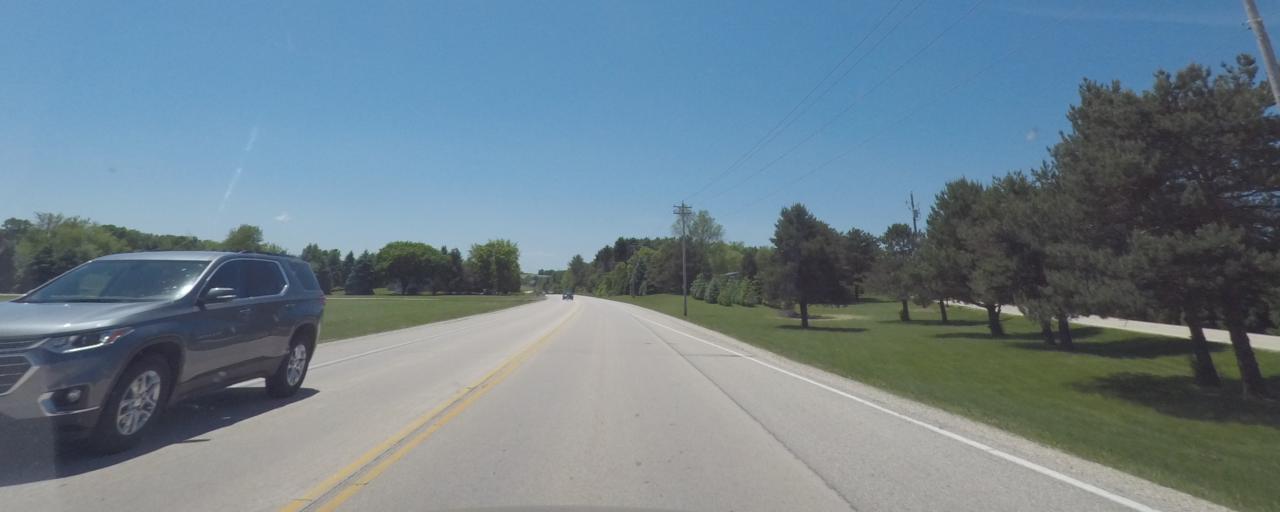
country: US
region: Wisconsin
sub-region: Ozaukee County
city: Kohler
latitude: 43.5361
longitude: -88.0922
